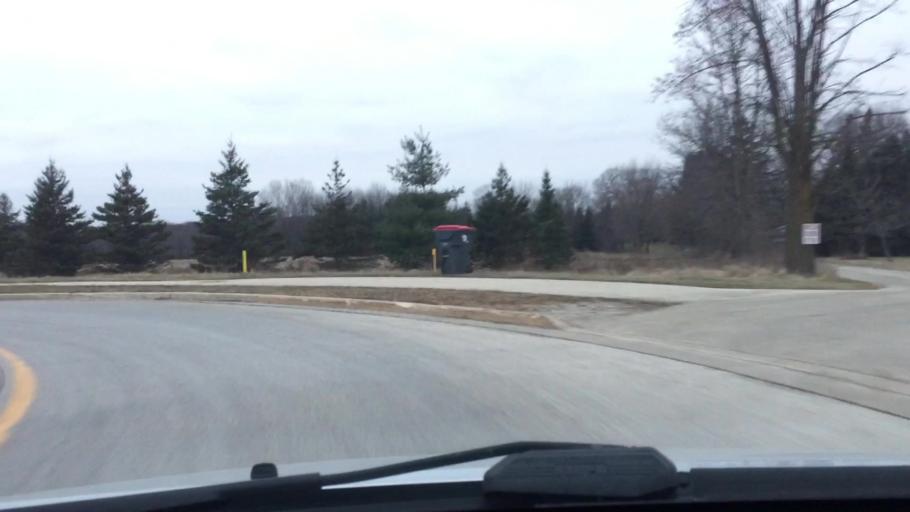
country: US
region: Wisconsin
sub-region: Jefferson County
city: Watertown
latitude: 43.1534
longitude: -88.7507
